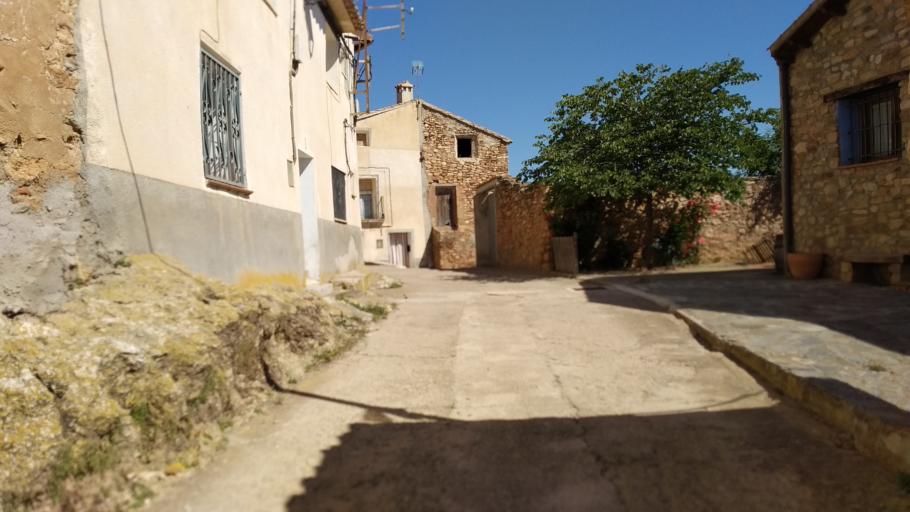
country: ES
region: Aragon
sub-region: Provincia de Teruel
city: Monforte de Moyuela
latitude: 41.0548
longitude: -1.0134
